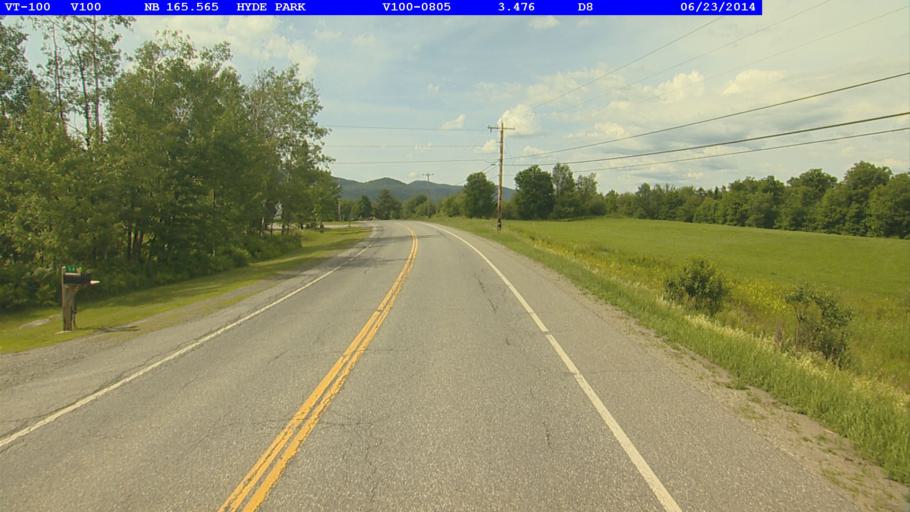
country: US
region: Vermont
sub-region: Lamoille County
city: Hyde Park
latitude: 44.6445
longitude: -72.5985
